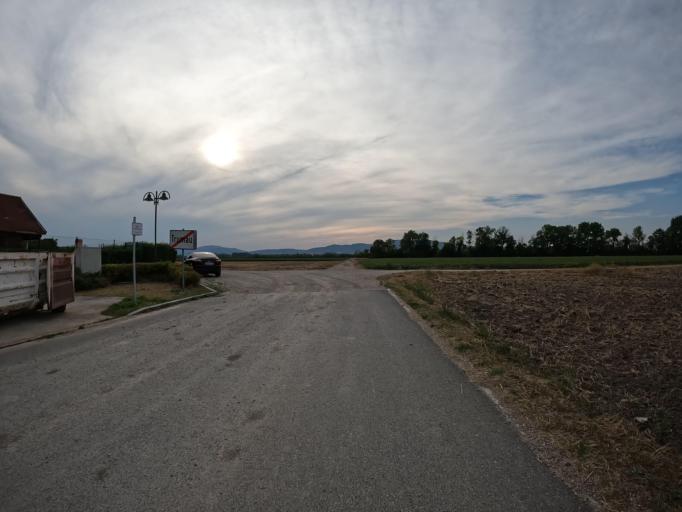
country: AT
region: Lower Austria
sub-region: Politischer Bezirk Baden
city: Trumau
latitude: 47.9991
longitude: 16.3360
